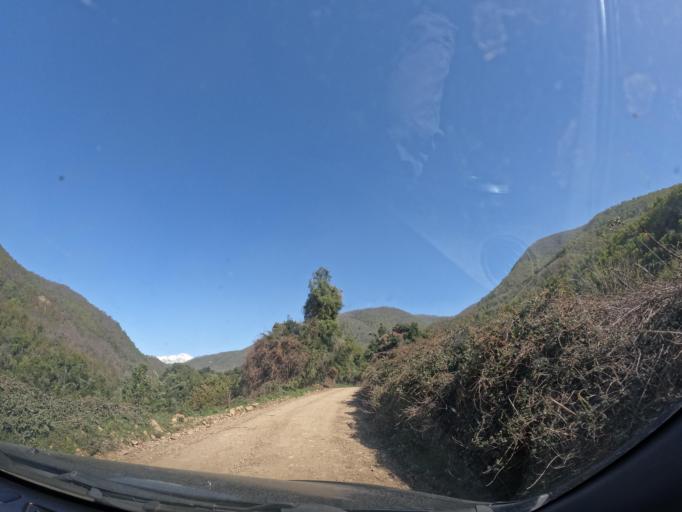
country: CL
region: Maule
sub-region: Provincia de Linares
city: Longavi
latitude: -36.2796
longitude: -71.4164
